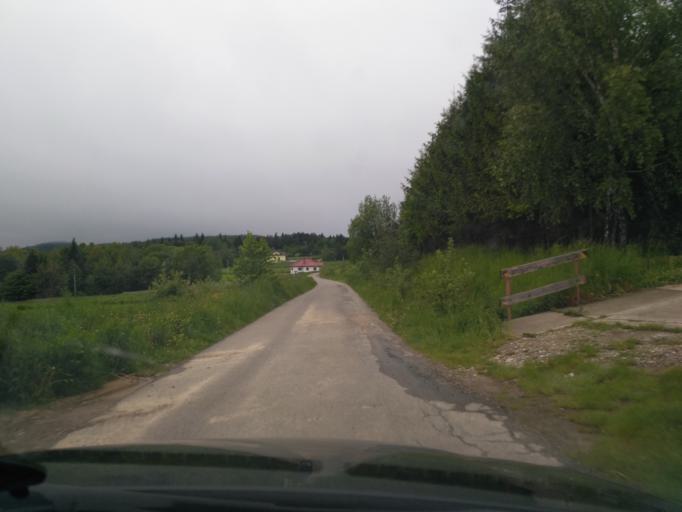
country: PL
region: Subcarpathian Voivodeship
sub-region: Powiat debicki
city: Jodlowa
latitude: 49.8563
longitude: 21.2499
